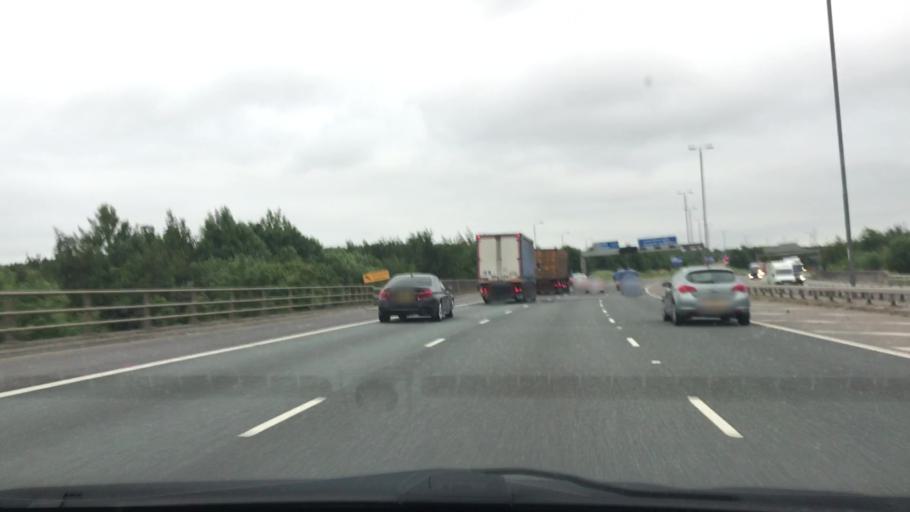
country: GB
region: England
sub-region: City and Borough of Leeds
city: Lofthouse
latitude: 53.7654
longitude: -1.4826
